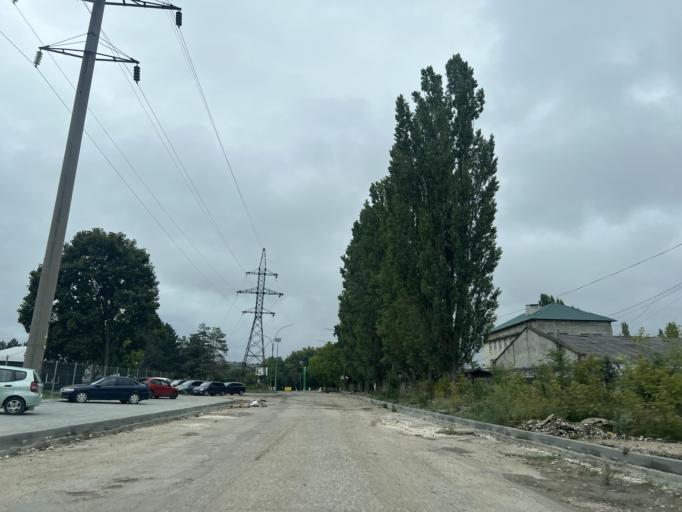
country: MD
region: Ungheni
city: Ungheni
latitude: 47.2228
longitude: 27.8083
